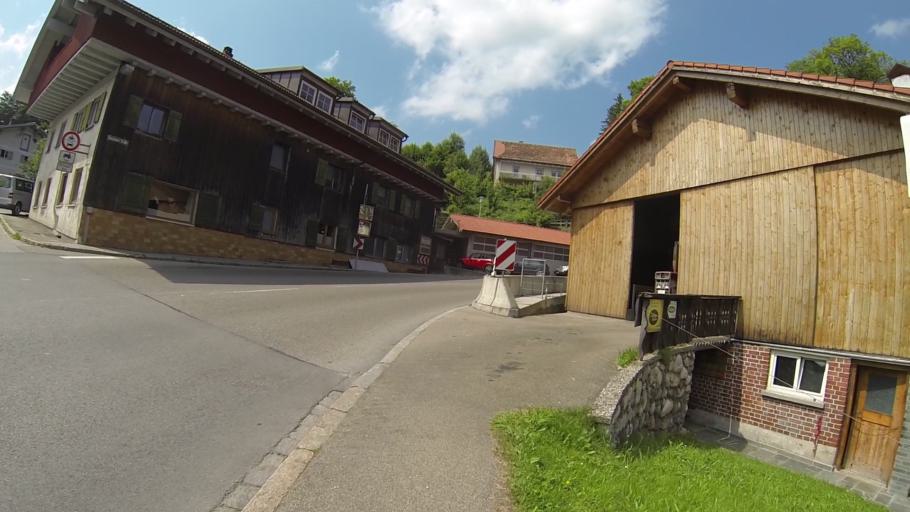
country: DE
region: Bavaria
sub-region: Swabia
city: Nesselwang
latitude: 47.6231
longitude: 10.4975
